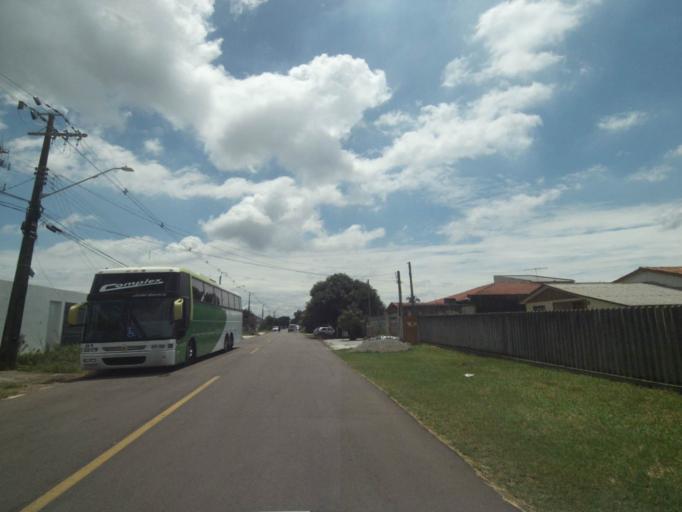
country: BR
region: Parana
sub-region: Pinhais
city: Pinhais
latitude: -25.4794
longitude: -49.1948
